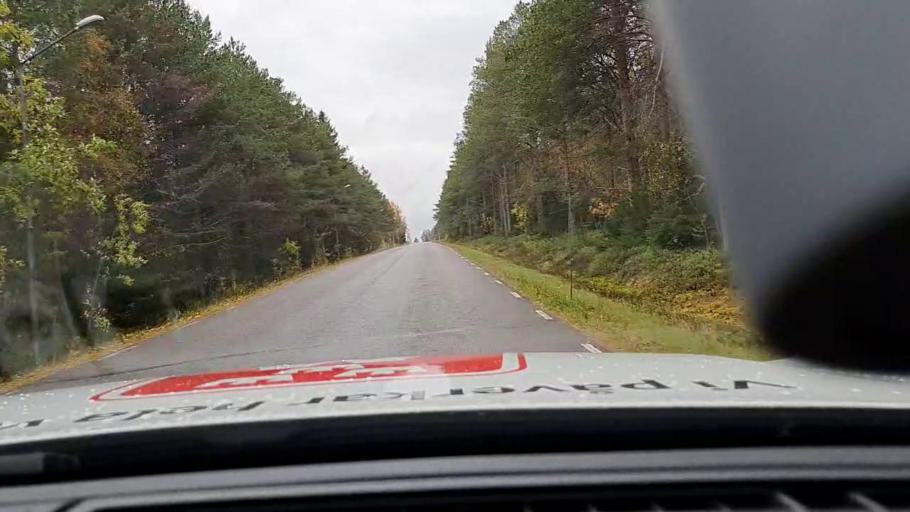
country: SE
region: Norrbotten
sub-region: Haparanda Kommun
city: Haparanda
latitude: 65.7878
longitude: 23.9212
